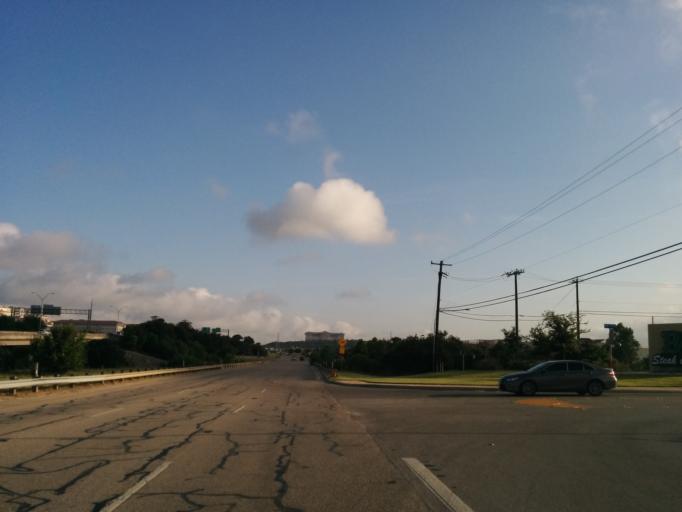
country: US
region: Texas
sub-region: Bexar County
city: Shavano Park
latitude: 29.6032
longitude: -98.6004
